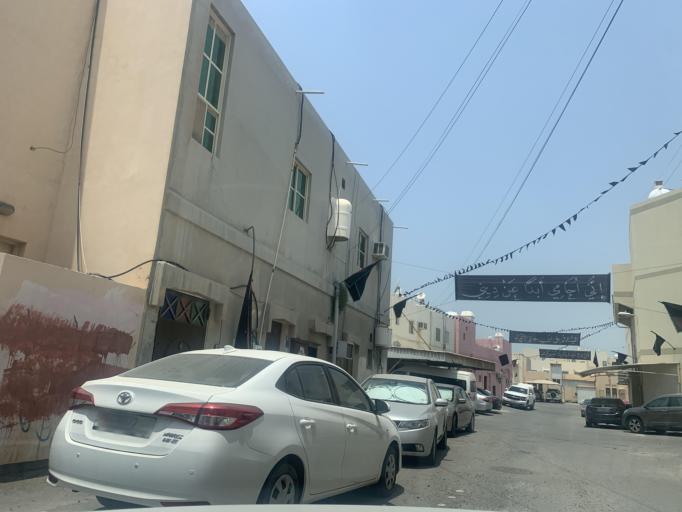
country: BH
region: Central Governorate
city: Madinat Hamad
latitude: 26.1437
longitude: 50.4616
